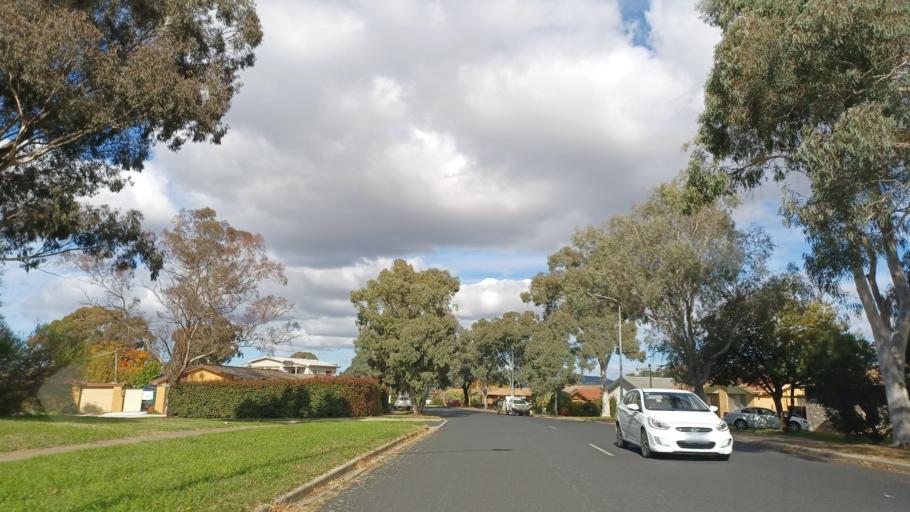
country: AU
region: Australian Capital Territory
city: Belconnen
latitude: -35.2069
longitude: 149.0706
